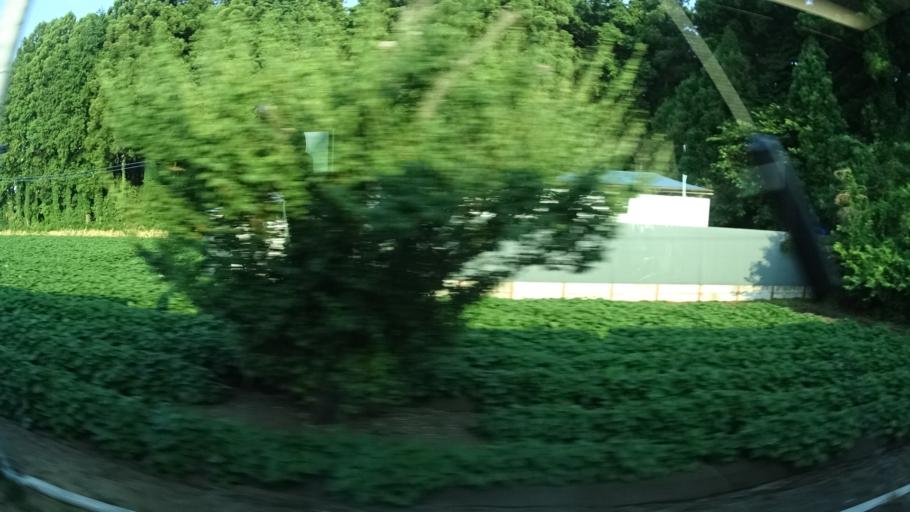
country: JP
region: Ibaraki
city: Funaishikawa
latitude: 36.4555
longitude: 140.5535
